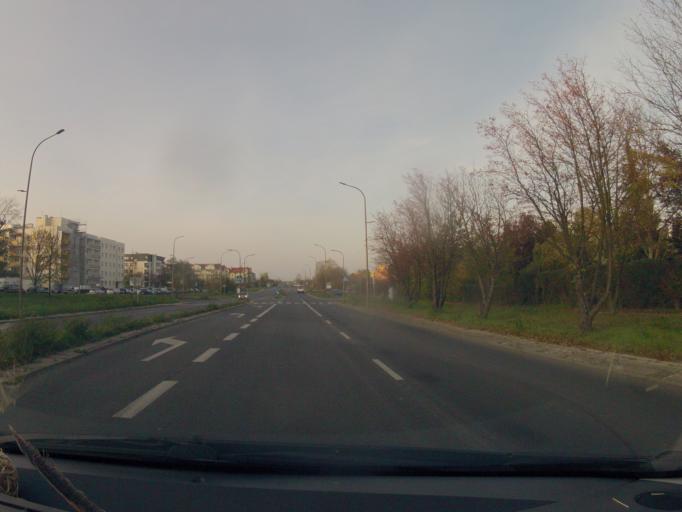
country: PL
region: Opole Voivodeship
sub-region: Powiat opolski
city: Opole
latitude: 50.6734
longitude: 17.9752
